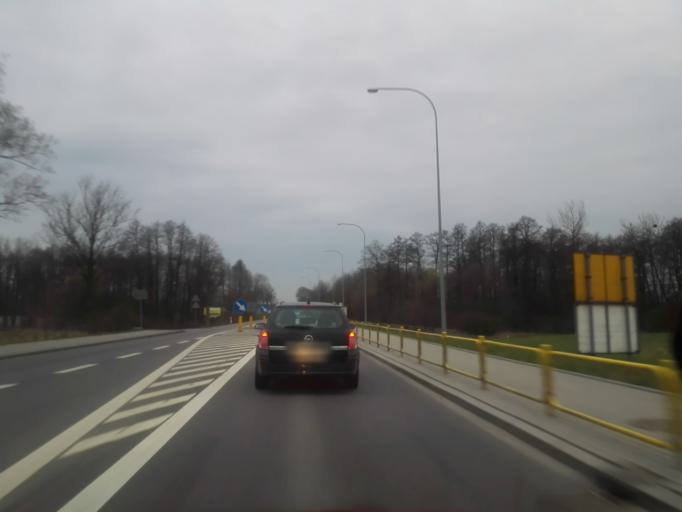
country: PL
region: Podlasie
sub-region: Powiat lomzynski
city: Piatnica
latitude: 53.2284
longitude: 22.1112
